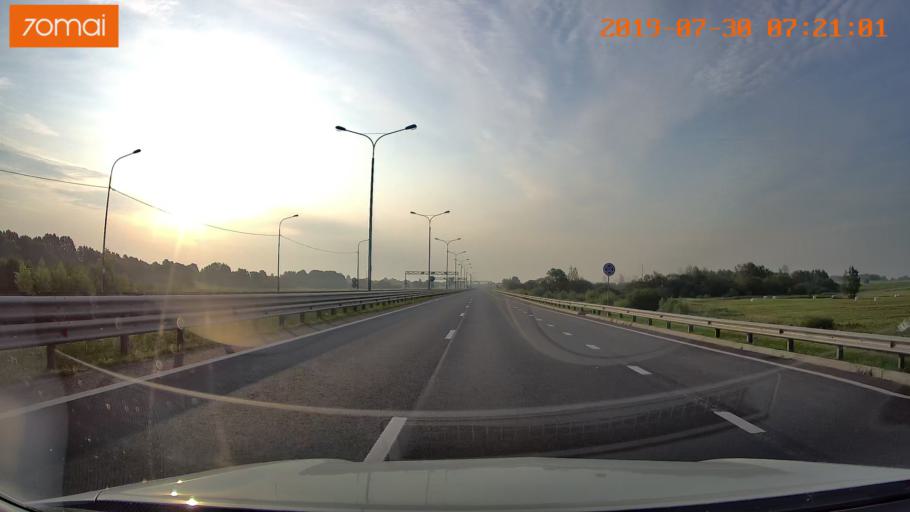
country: RU
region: Kaliningrad
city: Bol'shoe Isakovo
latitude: 54.6983
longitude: 20.7177
